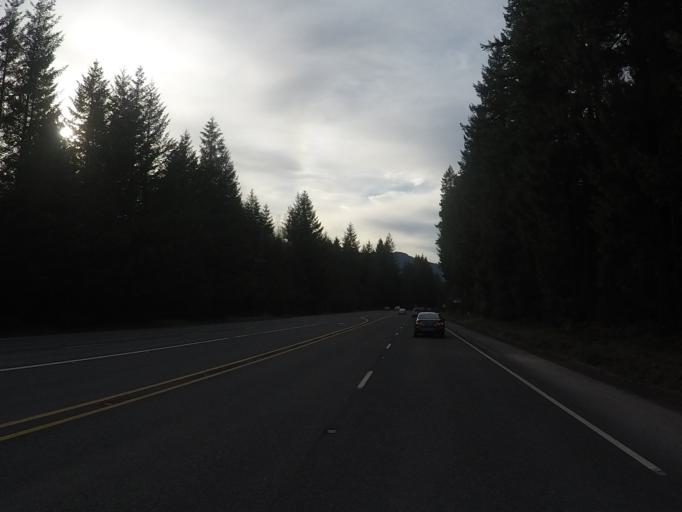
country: US
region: Oregon
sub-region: Clackamas County
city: Mount Hood Village
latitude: 45.3456
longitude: -121.9530
